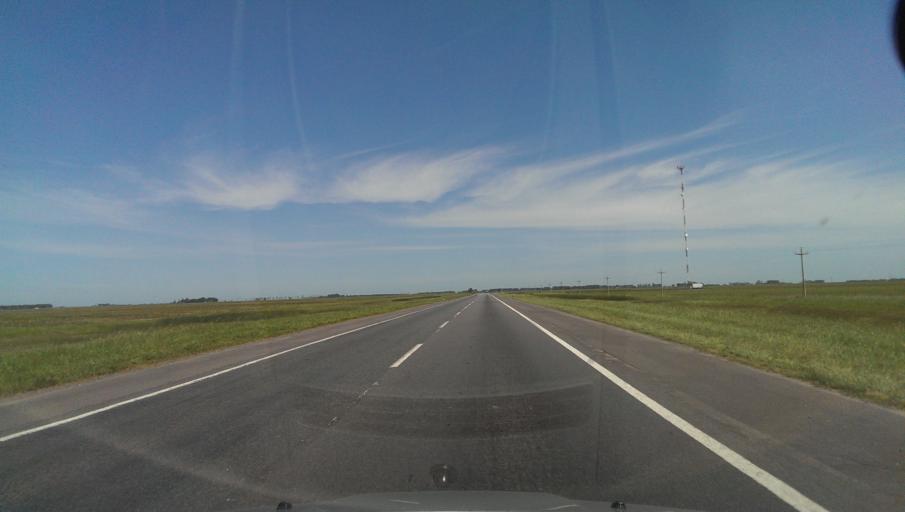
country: AR
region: Buenos Aires
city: San Miguel del Monte
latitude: -35.7249
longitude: -58.9079
